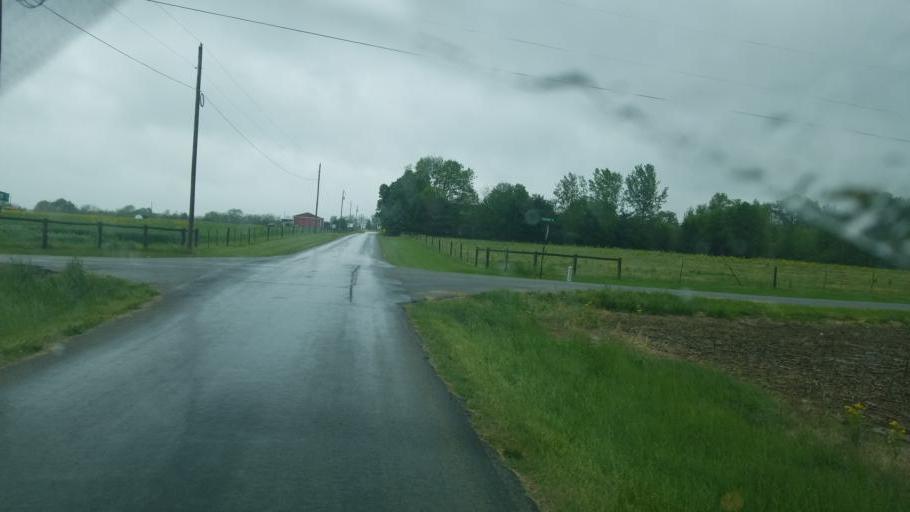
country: US
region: Ohio
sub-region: Highland County
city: Greenfield
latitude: 39.3343
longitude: -83.4352
